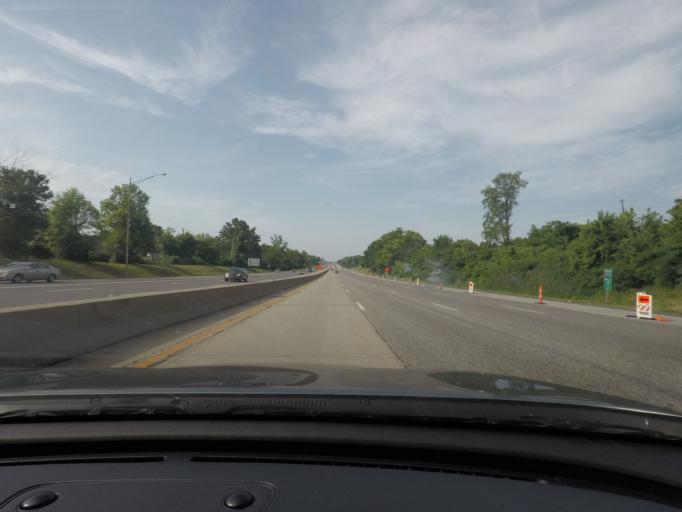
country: US
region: Missouri
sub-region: Saint Louis County
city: Maryland Heights
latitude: 38.7359
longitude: -90.4426
